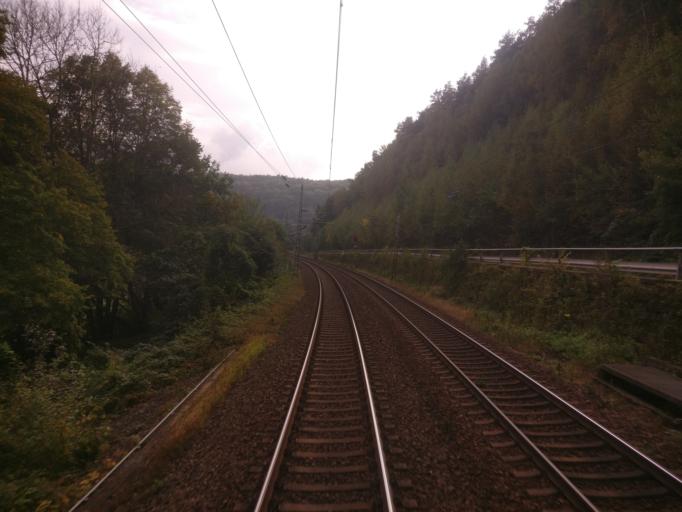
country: DE
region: Saxony
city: Konigstein
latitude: 50.9332
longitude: 14.0579
